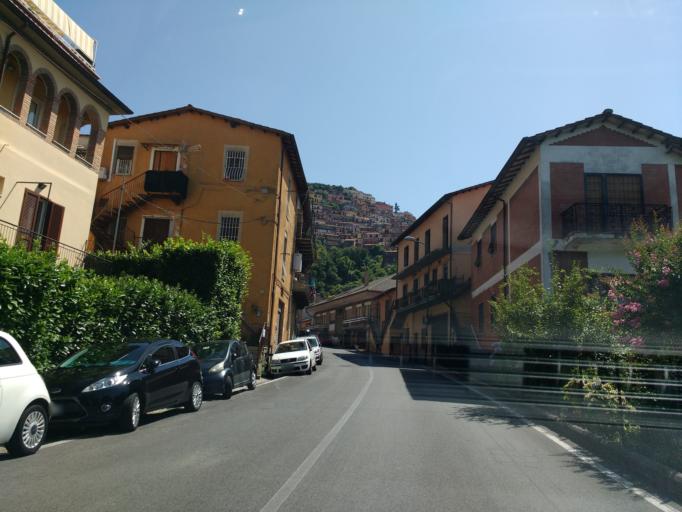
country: IT
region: Latium
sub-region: Citta metropolitana di Roma Capitale
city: Rocca di Papa
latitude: 41.7648
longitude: 12.7106
